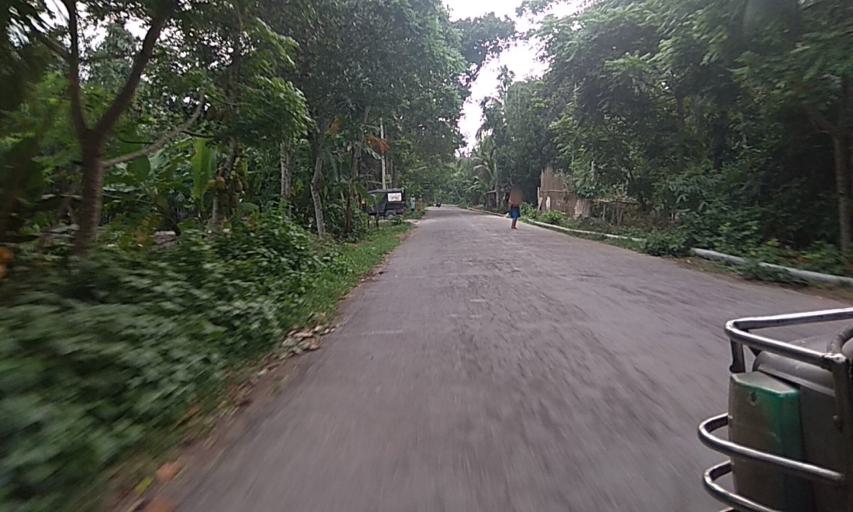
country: BD
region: Dhaka
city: Dohar
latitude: 23.4602
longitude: 89.9882
